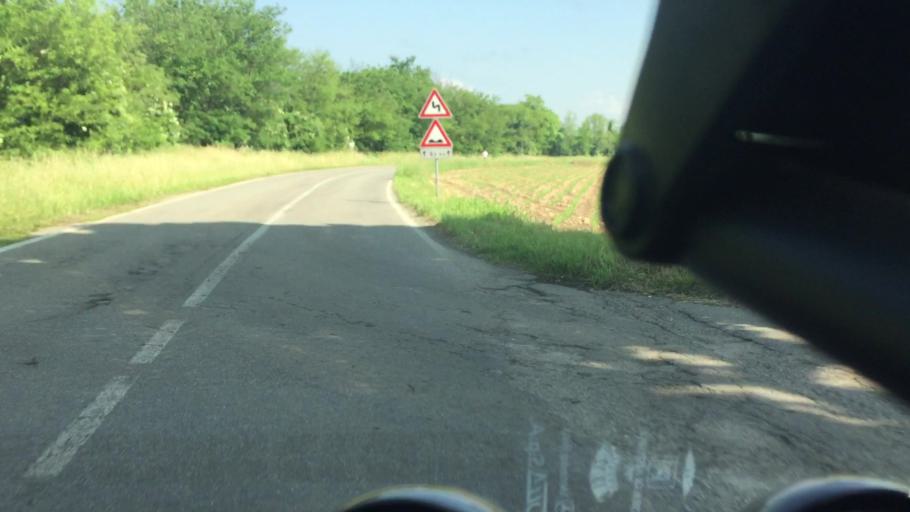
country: IT
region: Lombardy
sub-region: Provincia di Bergamo
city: Badalasco
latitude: 45.5499
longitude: 9.5666
